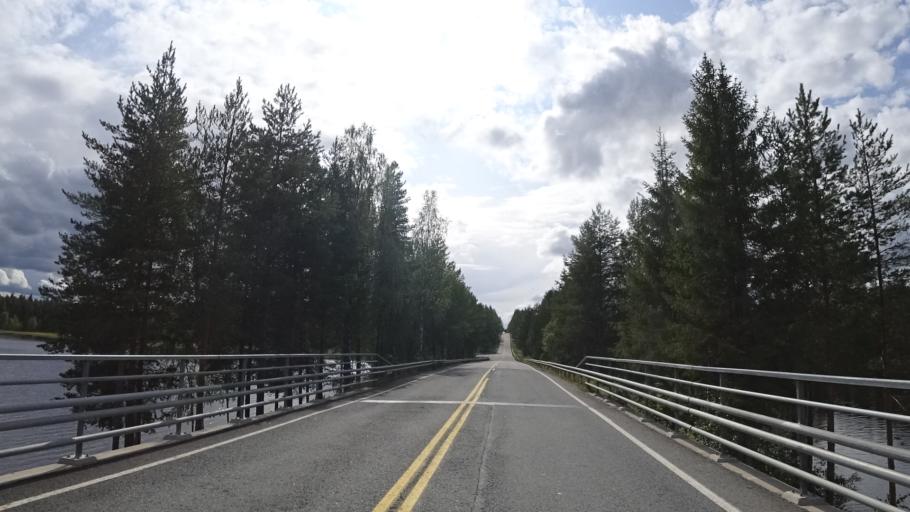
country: FI
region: North Karelia
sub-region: Joensuu
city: Ilomantsi
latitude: 62.7582
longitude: 31.0109
